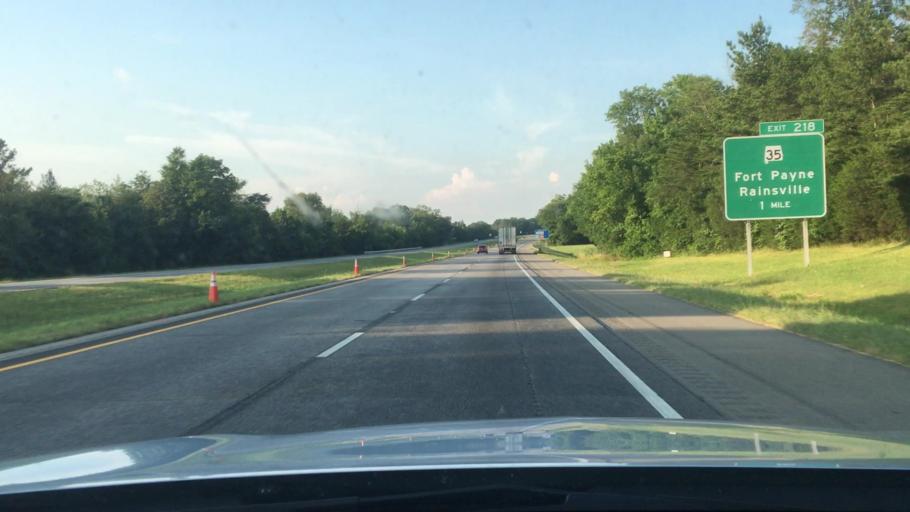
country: US
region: Alabama
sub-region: DeKalb County
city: Fort Payne
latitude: 34.4245
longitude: -85.7636
